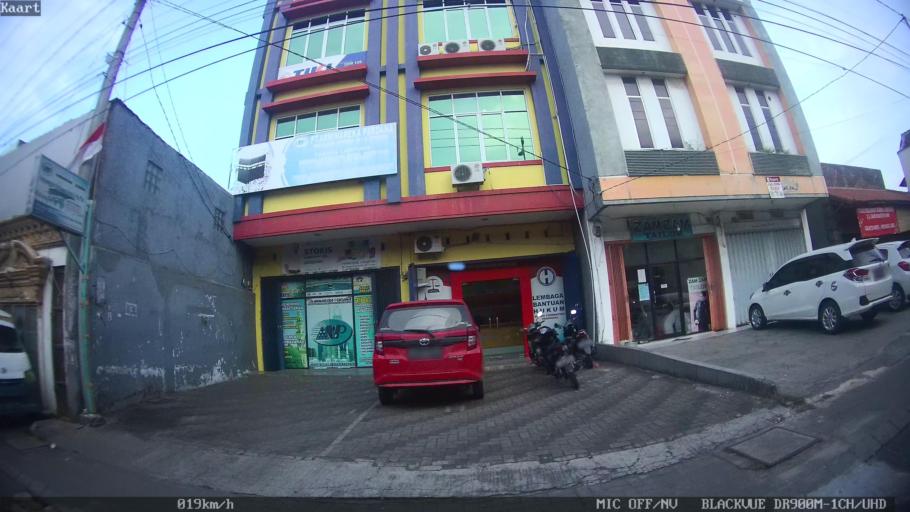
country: ID
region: Lampung
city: Bandarlampung
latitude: -5.4095
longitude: 105.2683
